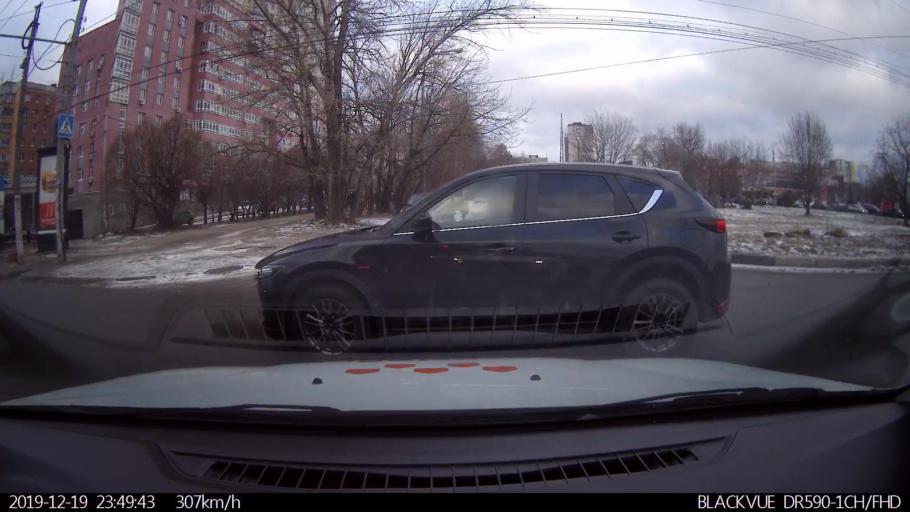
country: RU
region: Jaroslavl
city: Breytovo
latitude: 58.4210
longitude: 37.9482
